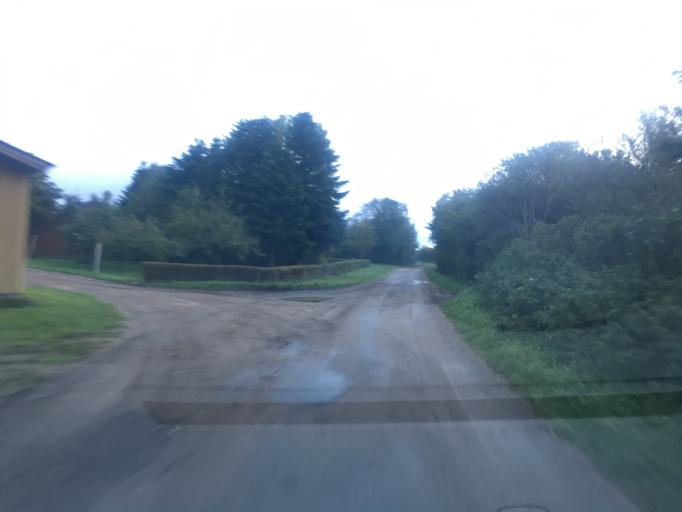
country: DK
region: South Denmark
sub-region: Tonder Kommune
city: Logumkloster
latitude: 54.9862
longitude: 9.0153
